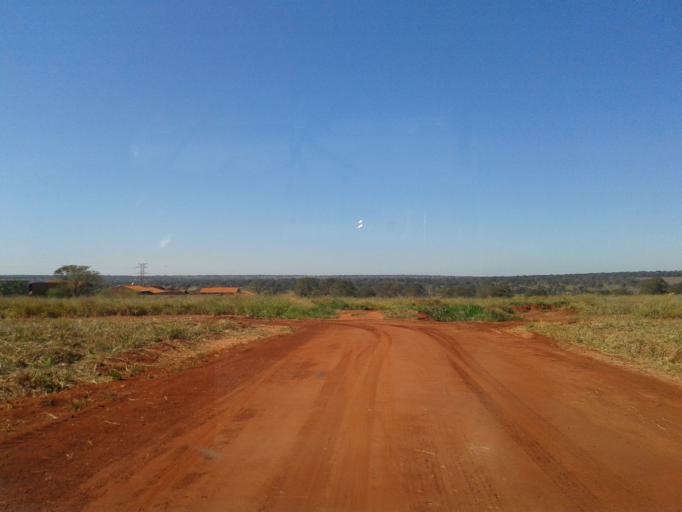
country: BR
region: Minas Gerais
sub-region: Santa Vitoria
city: Santa Vitoria
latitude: -18.8610
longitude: -50.1209
